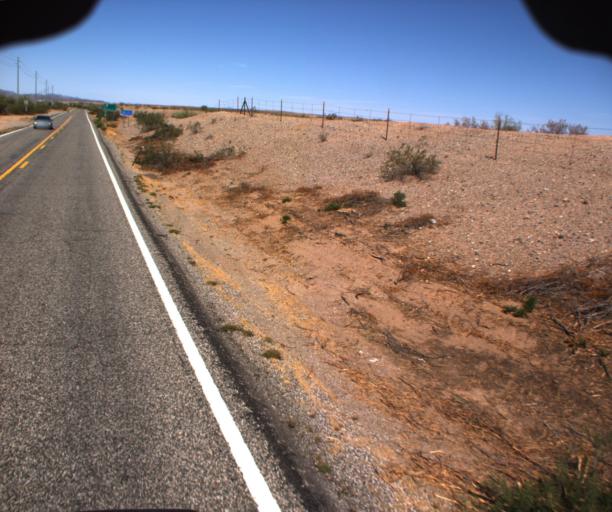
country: US
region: Arizona
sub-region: La Paz County
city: Cienega Springs
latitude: 33.9934
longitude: -114.1313
